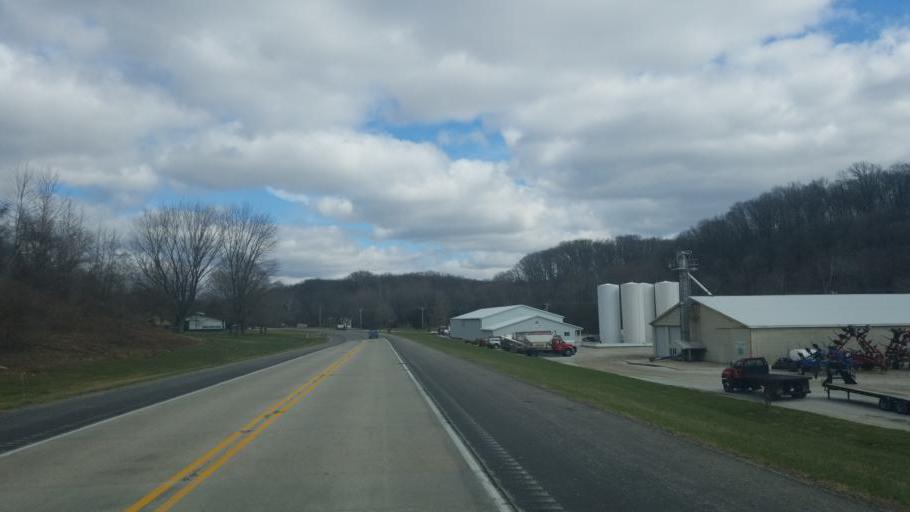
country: US
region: Indiana
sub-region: Parke County
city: Montezuma
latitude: 39.7750
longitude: -87.3215
